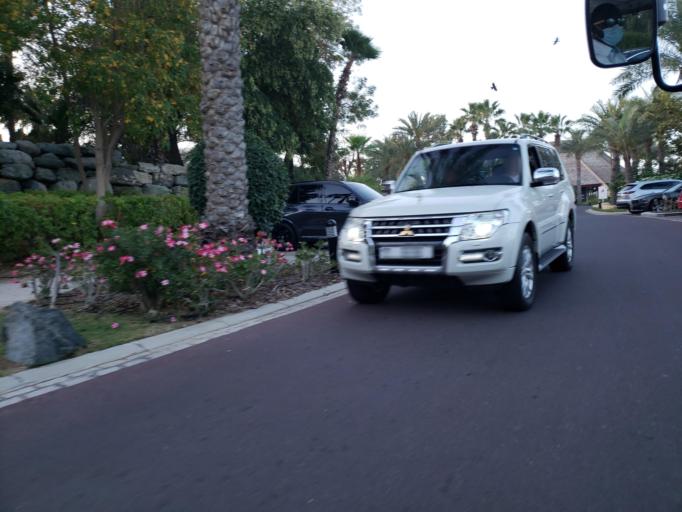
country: AE
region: Dubai
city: Dubai
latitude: 24.9865
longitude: 55.0219
